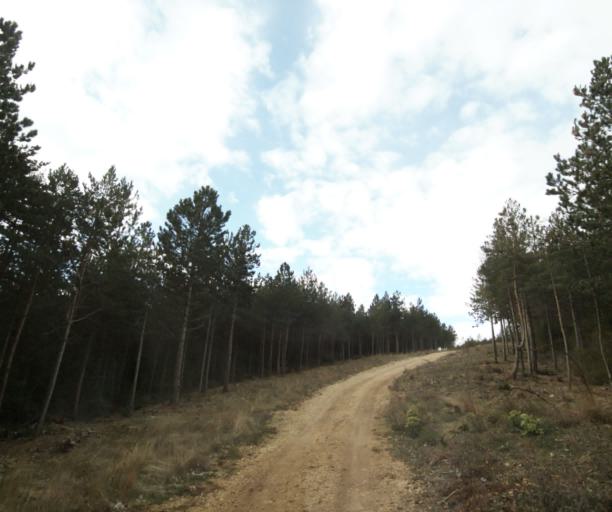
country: FR
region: Midi-Pyrenees
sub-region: Departement de l'Aveyron
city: Millau
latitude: 44.1219
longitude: 3.1531
